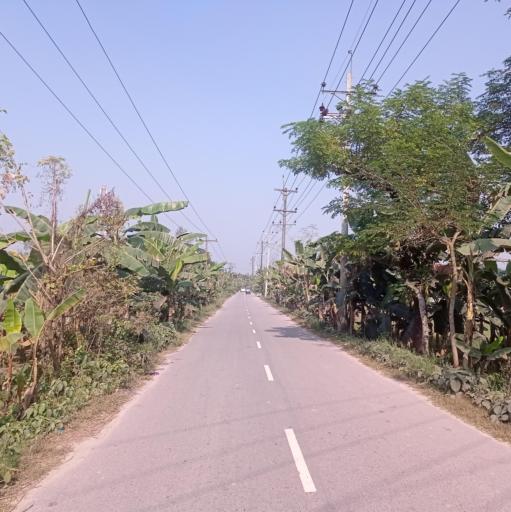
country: BD
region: Dhaka
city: Narsingdi
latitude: 24.0783
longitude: 90.6939
